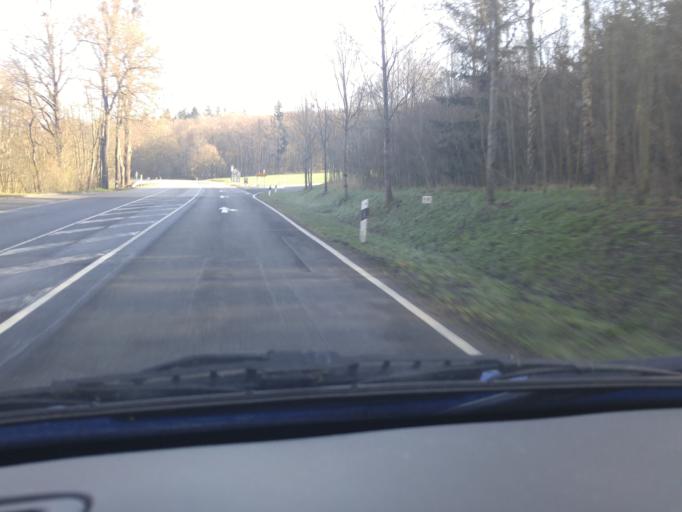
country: DE
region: Hesse
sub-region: Regierungsbezirk Giessen
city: Lauterbach
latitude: 50.6005
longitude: 9.3921
